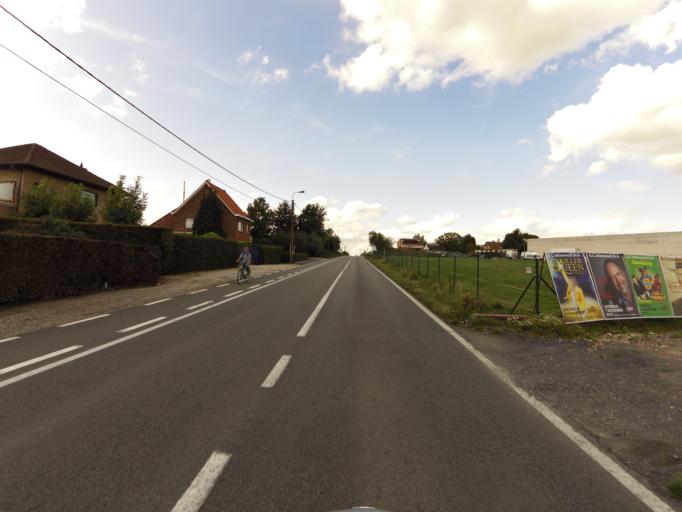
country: BE
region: Flanders
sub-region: Provincie West-Vlaanderen
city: Waregem
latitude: 50.8645
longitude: 3.4462
